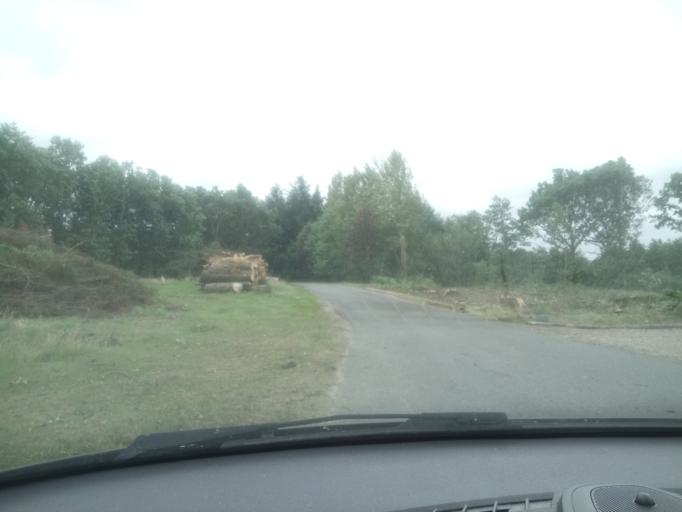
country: DK
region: Central Jutland
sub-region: Ringkobing-Skjern Kommune
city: Videbaek
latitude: 55.9530
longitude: 8.6725
